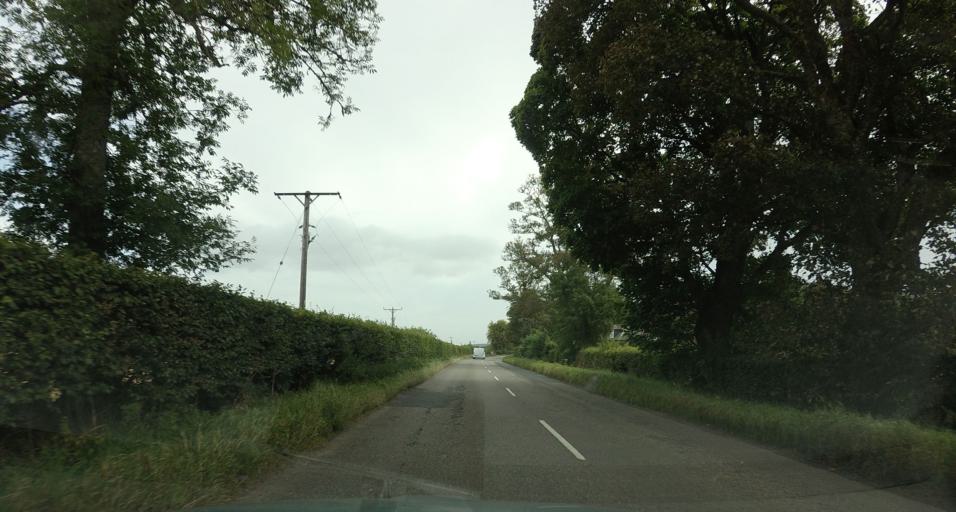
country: GB
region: Scotland
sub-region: Aberdeenshire
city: Kemnay
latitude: 57.2244
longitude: -2.5138
